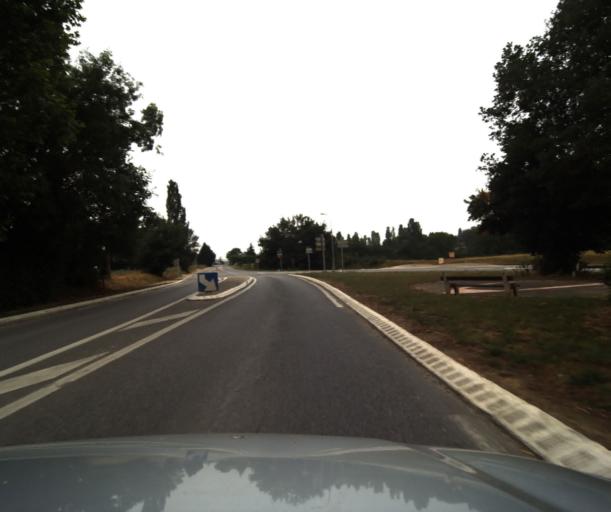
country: FR
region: Midi-Pyrenees
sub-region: Departement du Gers
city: Gimont
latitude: 43.7248
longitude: 0.8740
